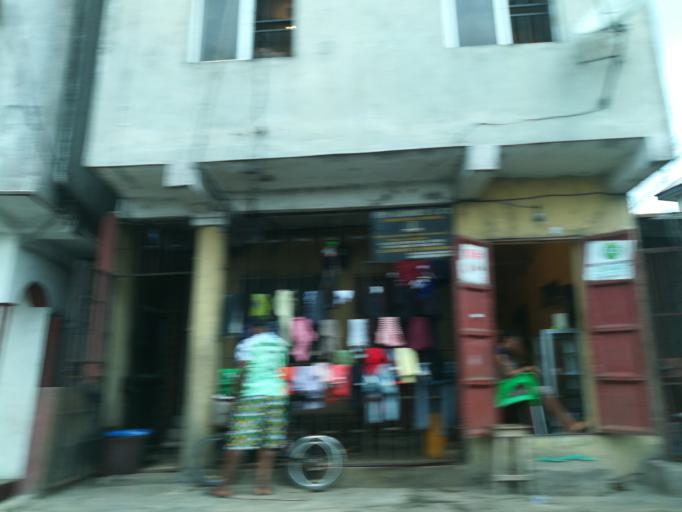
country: NG
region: Rivers
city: Port Harcourt
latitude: 4.8025
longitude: 6.9867
